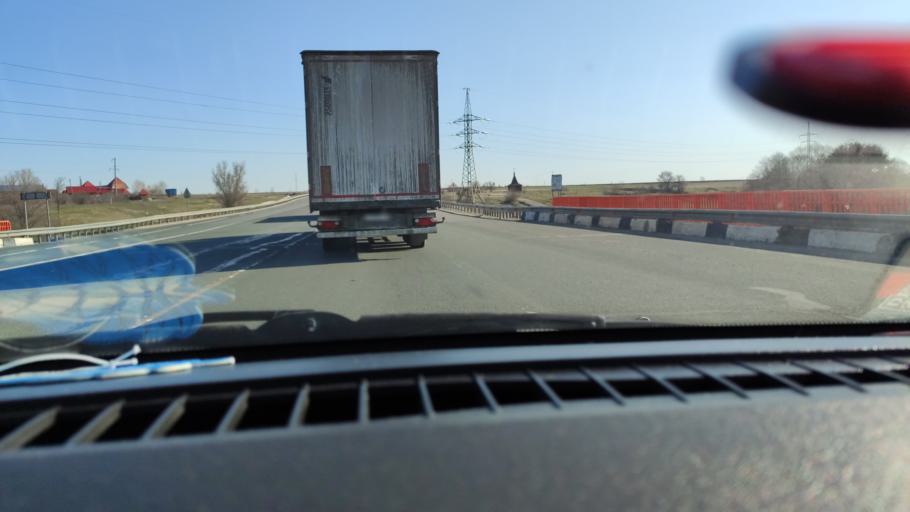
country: RU
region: Samara
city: Varlamovo
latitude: 53.2057
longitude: 48.3849
